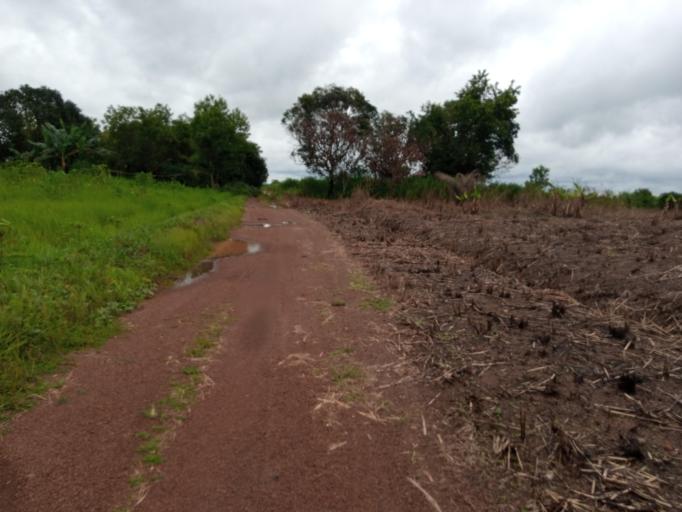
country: SL
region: Southern Province
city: Largo
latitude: 8.1972
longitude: -12.0484
